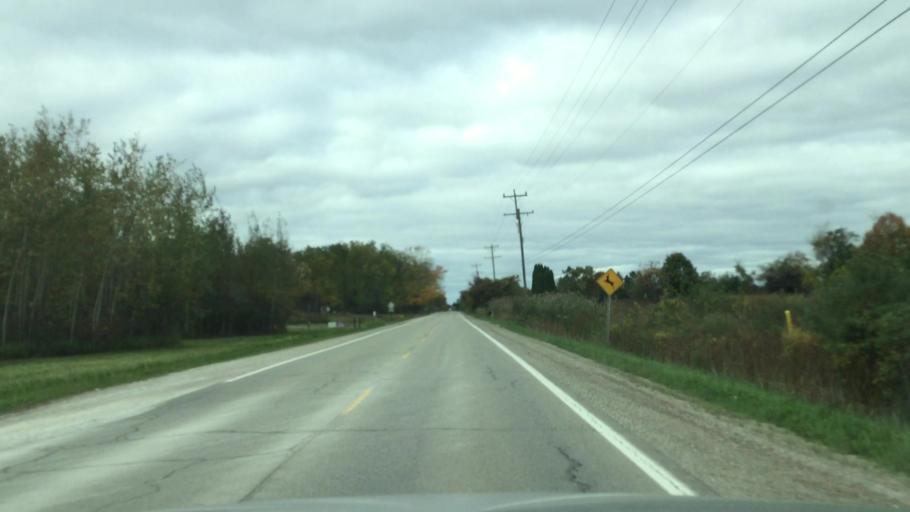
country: US
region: Michigan
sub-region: Macomb County
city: Armada
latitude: 42.8060
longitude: -82.9035
